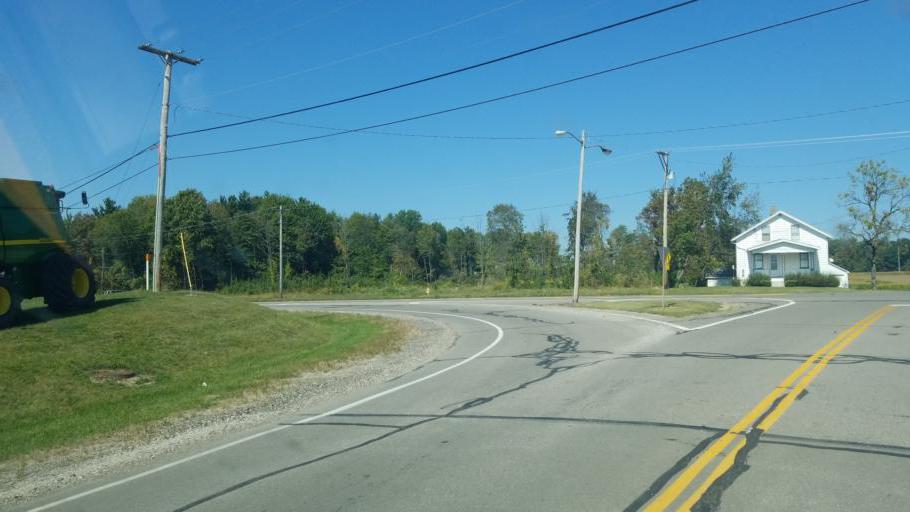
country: US
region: Ohio
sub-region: Richland County
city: Ontario
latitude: 40.7752
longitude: -82.6099
